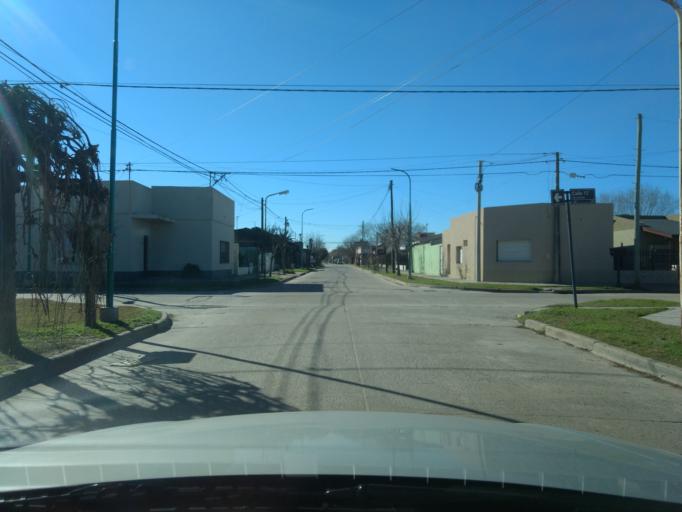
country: AR
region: Buenos Aires
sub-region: Partido de Navarro
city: Navarro
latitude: -35.0007
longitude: -59.2742
